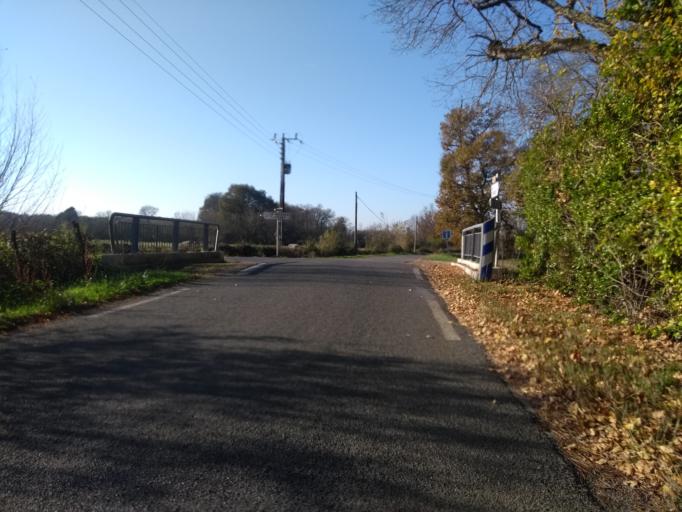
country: FR
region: Aquitaine
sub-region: Departement de la Gironde
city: Ayguemorte-les-Graves
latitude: 44.7264
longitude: -0.4896
